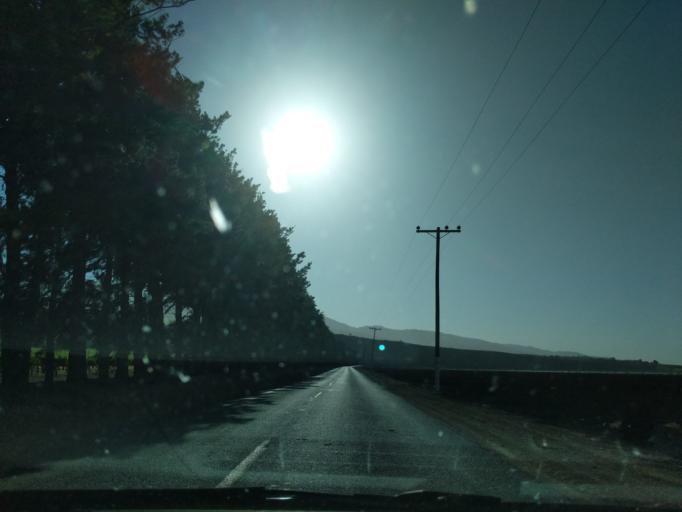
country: US
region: California
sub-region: Monterey County
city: Soledad
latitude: 36.4101
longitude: -121.3823
